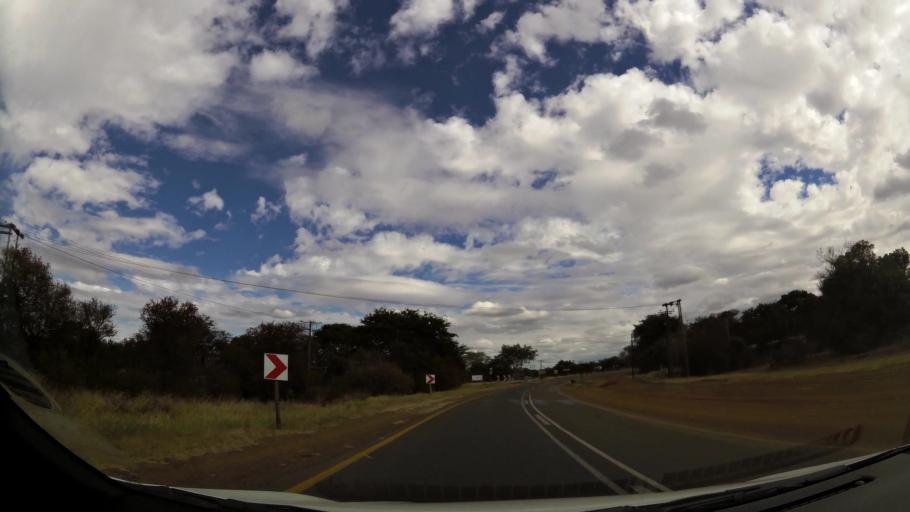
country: ZA
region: Limpopo
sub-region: Waterberg District Municipality
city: Warmbaths
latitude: -24.9017
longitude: 28.2785
